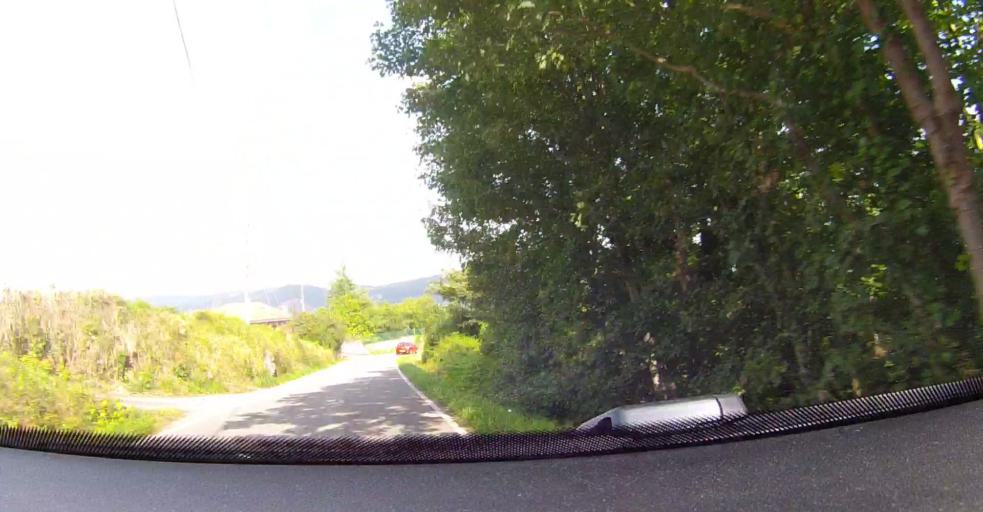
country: ES
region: Asturias
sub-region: Province of Asturias
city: Villaviciosa
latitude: 43.4859
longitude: -5.4189
